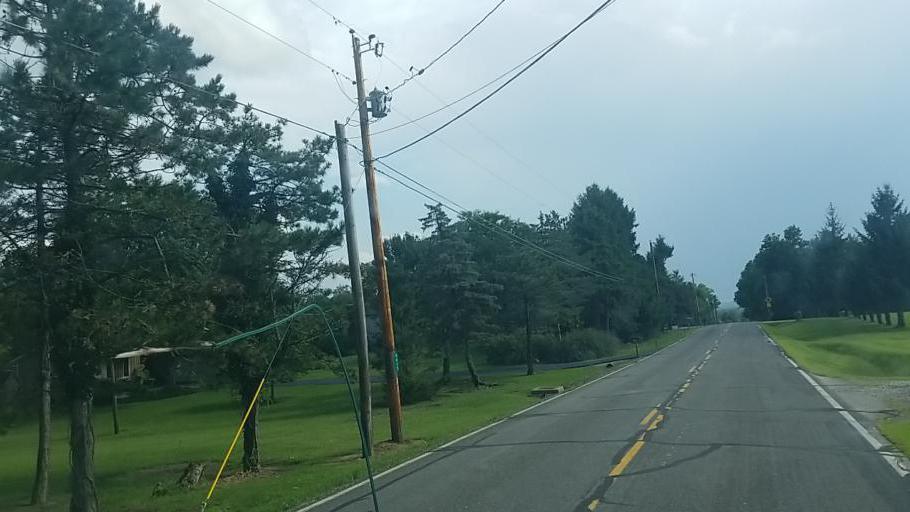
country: US
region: Ohio
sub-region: Medina County
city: Westfield Center
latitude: 41.0164
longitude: -81.9668
